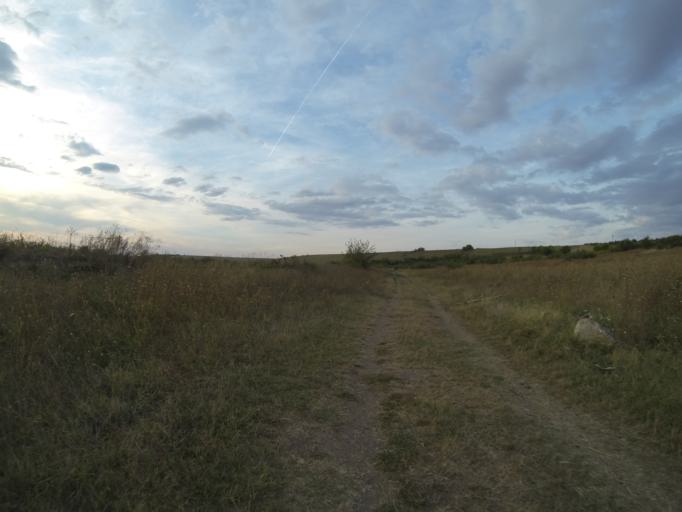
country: RO
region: Dolj
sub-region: Comuna Ceratu
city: Ceratu
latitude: 44.0898
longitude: 23.6695
